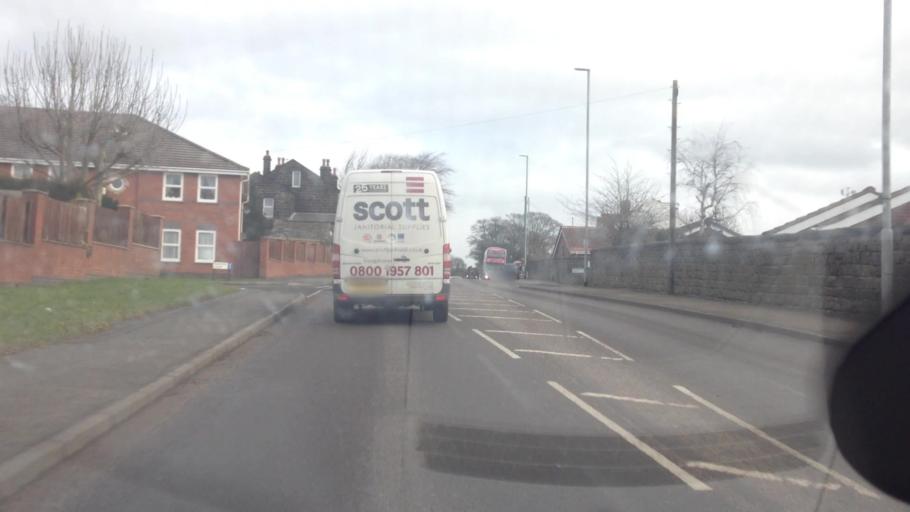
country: GB
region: England
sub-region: City and Borough of Leeds
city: Yeadon
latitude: 53.8621
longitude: -1.6737
